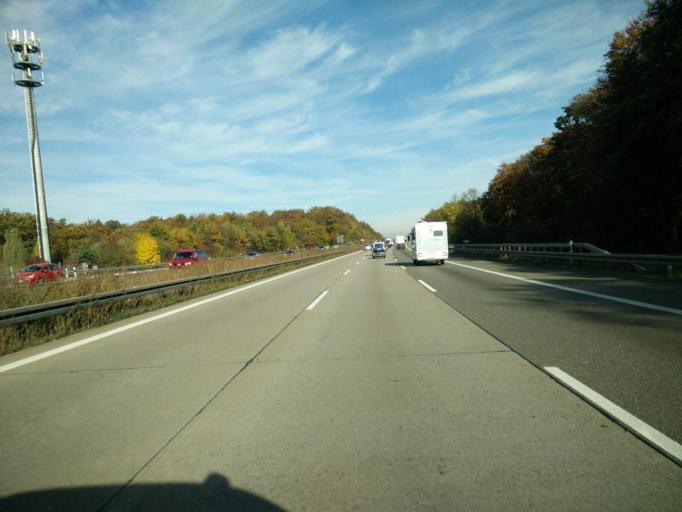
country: DE
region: Baden-Wuerttemberg
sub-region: Regierungsbezirk Stuttgart
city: Sindelfingen
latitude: 48.7435
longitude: 9.0351
